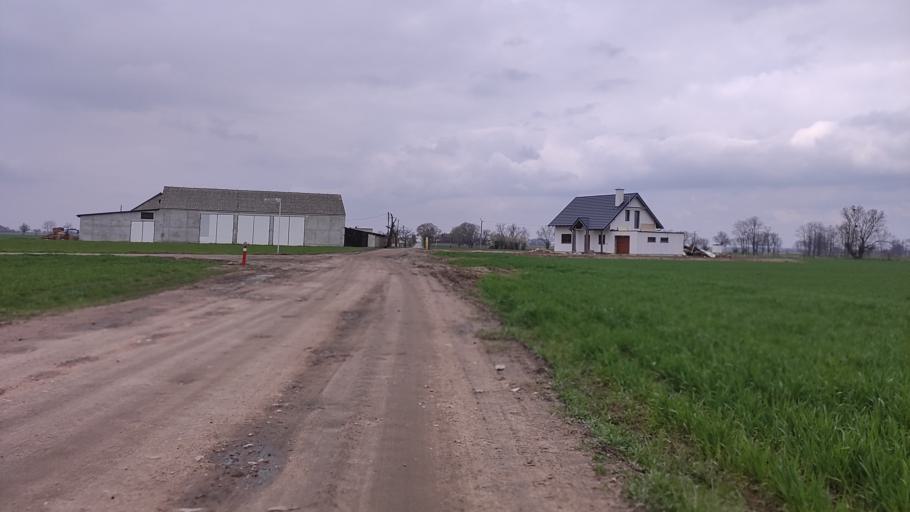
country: PL
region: Greater Poland Voivodeship
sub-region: Powiat poznanski
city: Swarzedz
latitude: 52.4057
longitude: 17.1403
